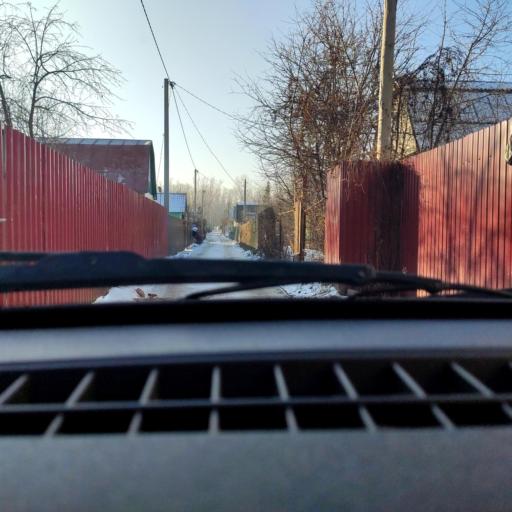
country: RU
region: Bashkortostan
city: Ufa
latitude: 54.7717
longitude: 55.9395
